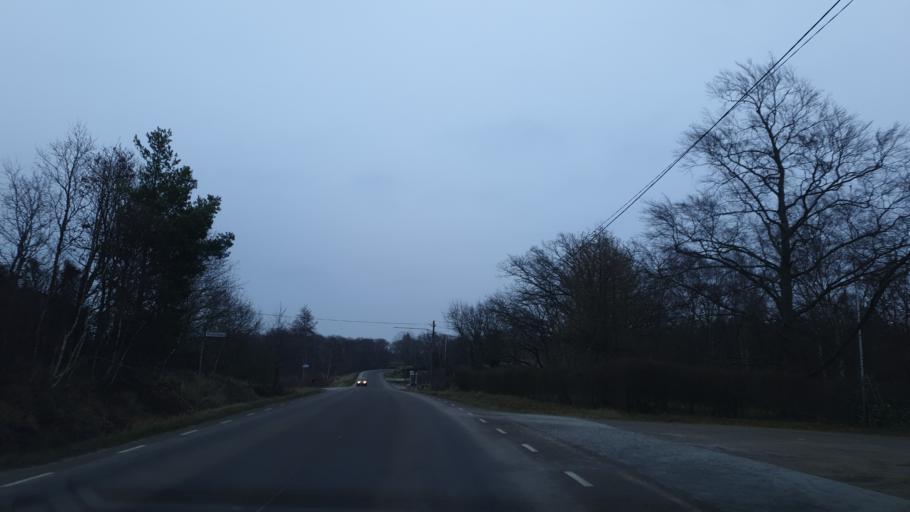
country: SE
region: Blekinge
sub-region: Karlskrona Kommun
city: Sturko
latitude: 56.1106
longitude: 15.7096
